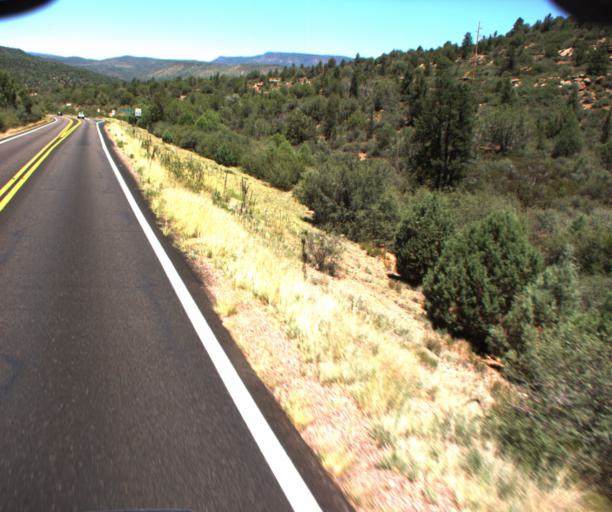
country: US
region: Arizona
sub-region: Gila County
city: Payson
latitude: 34.2927
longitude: -111.3484
